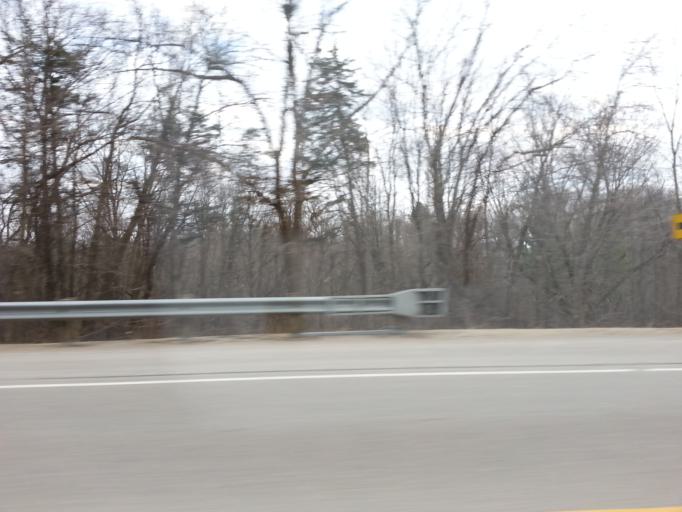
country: US
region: Wisconsin
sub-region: Pierce County
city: Ellsworth
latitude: 44.7308
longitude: -92.4904
